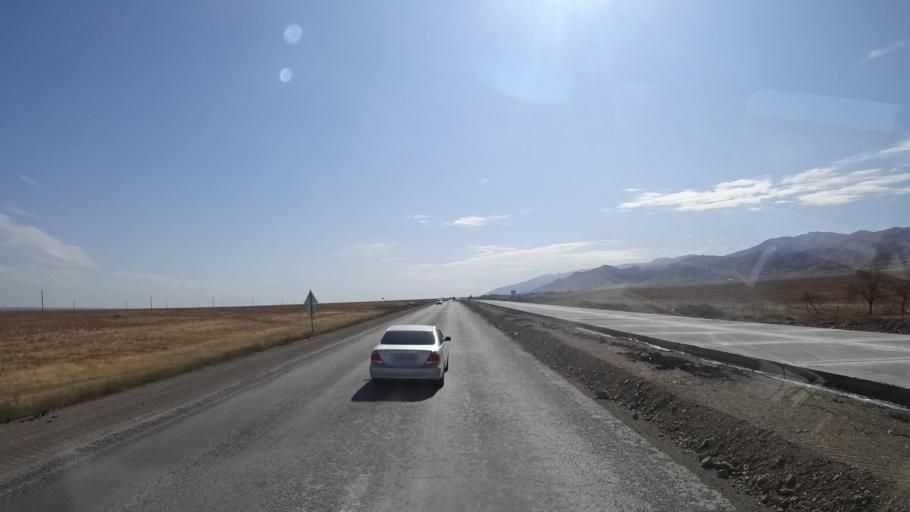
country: KG
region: Chuy
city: Ivanovka
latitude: 43.3979
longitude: 75.1213
